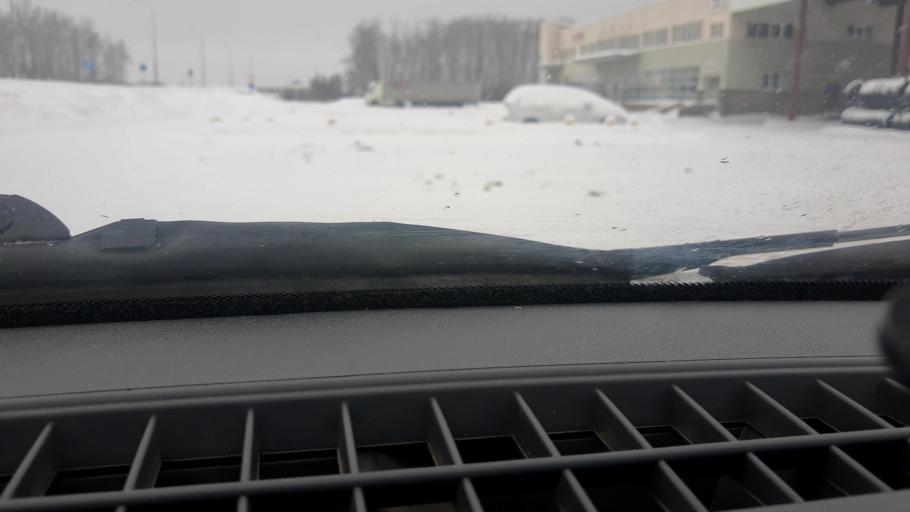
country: RU
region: Bashkortostan
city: Kabakovo
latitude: 54.6528
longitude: 56.1026
